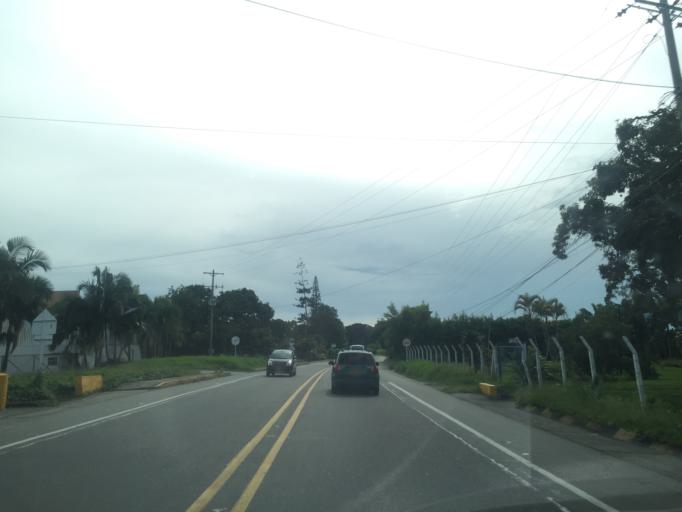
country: CO
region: Quindio
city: La Tebaida
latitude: 4.4857
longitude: -75.7460
